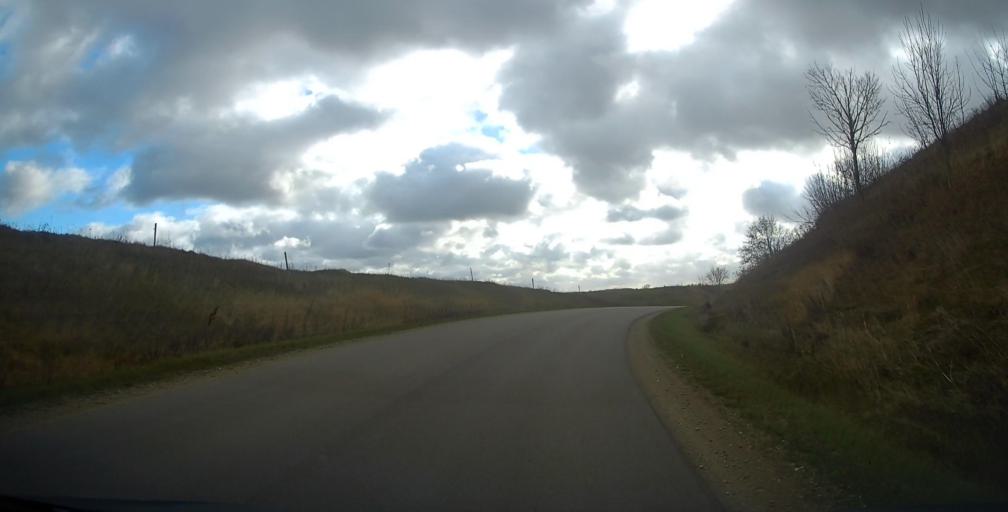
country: PL
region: Podlasie
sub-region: Suwalki
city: Suwalki
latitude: 54.3411
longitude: 22.8603
